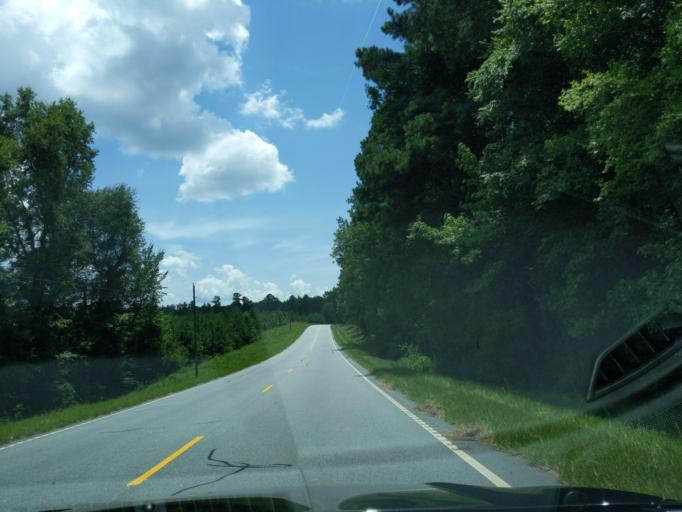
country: US
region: South Carolina
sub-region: Greenwood County
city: Ninety Six
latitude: 34.0115
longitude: -82.0419
